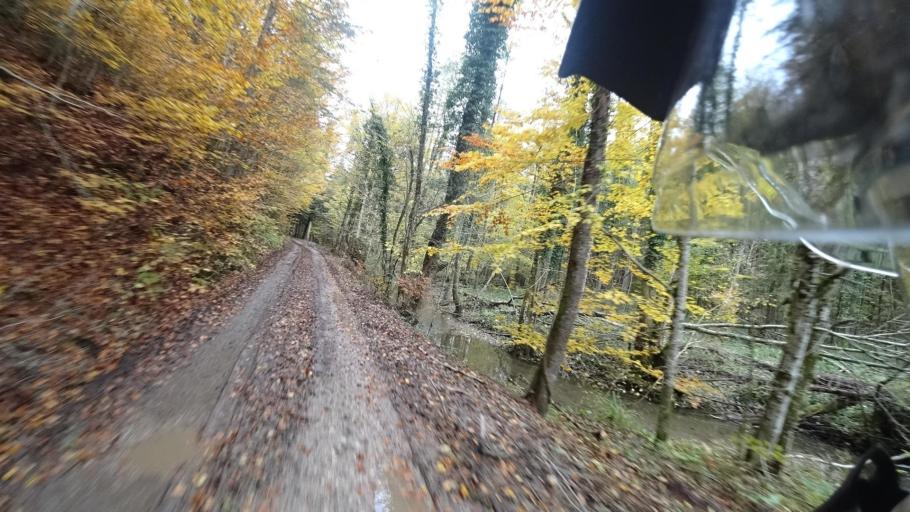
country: SI
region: Kostel
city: Kostel
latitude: 45.4359
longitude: 14.9574
